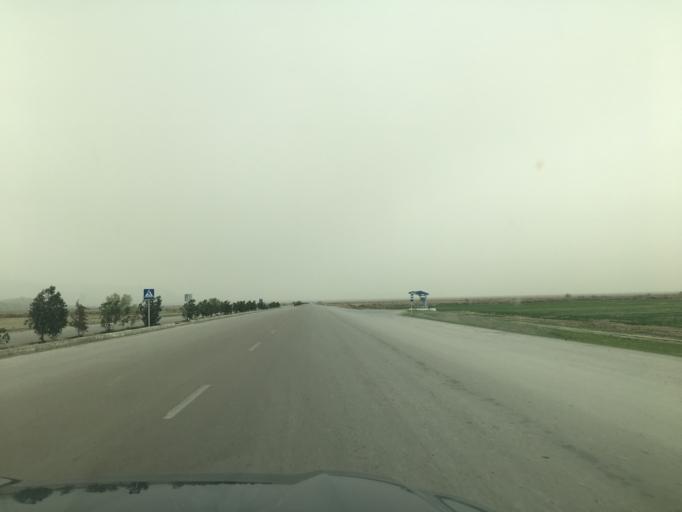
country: TM
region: Ahal
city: Baharly
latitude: 38.3285
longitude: 57.5838
